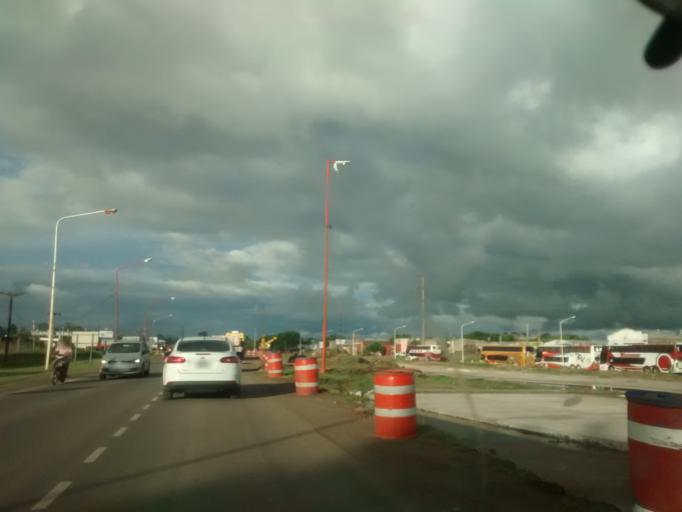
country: AR
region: Chaco
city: Fontana
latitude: -27.4446
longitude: -59.0221
